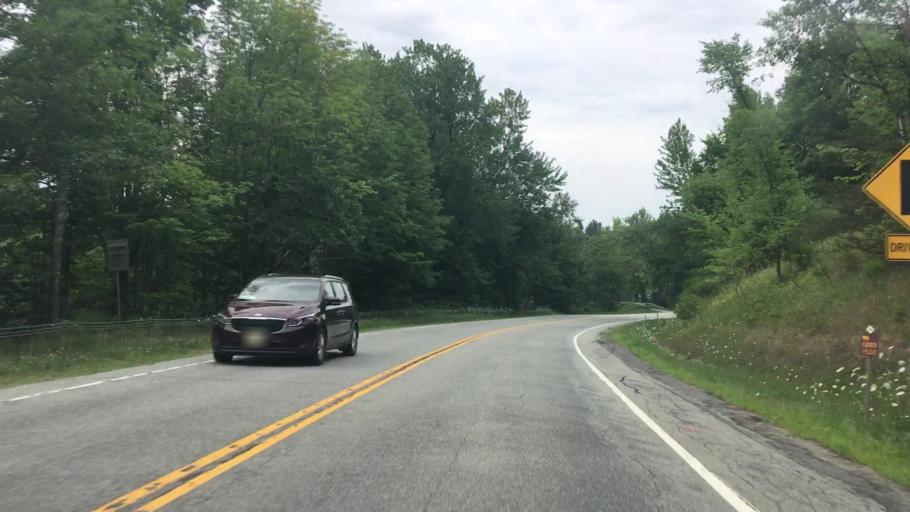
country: US
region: New York
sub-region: Essex County
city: Lake Placid
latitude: 44.2775
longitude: -73.7900
